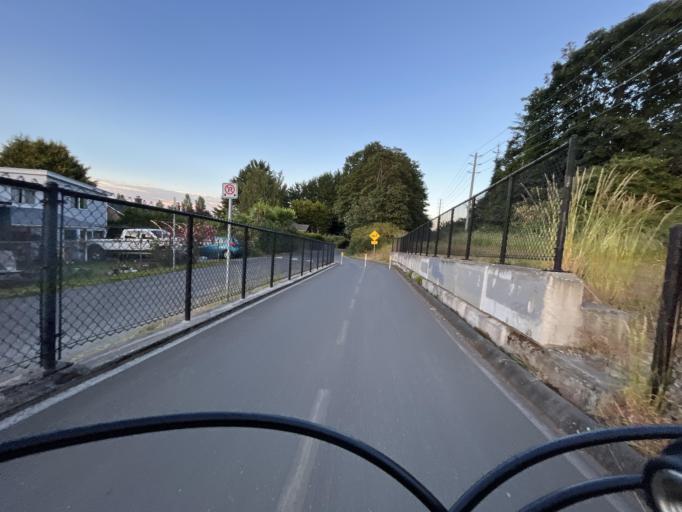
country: CA
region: British Columbia
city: Victoria
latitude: 48.4381
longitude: -123.4083
